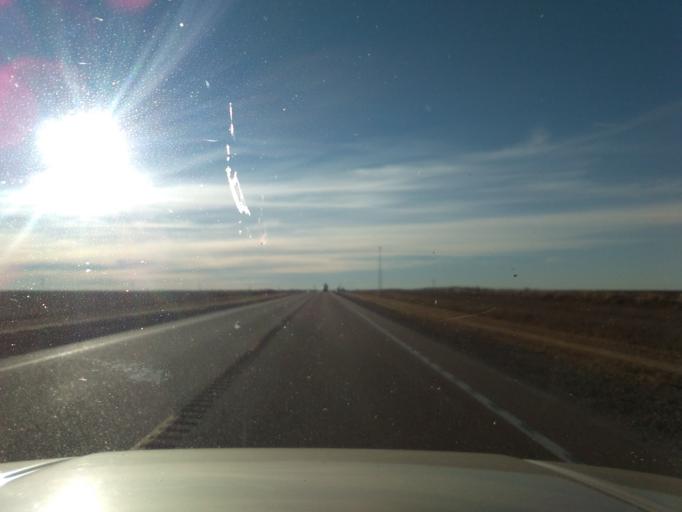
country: US
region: Kansas
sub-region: Sheridan County
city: Hoxie
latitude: 39.4835
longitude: -100.7086
